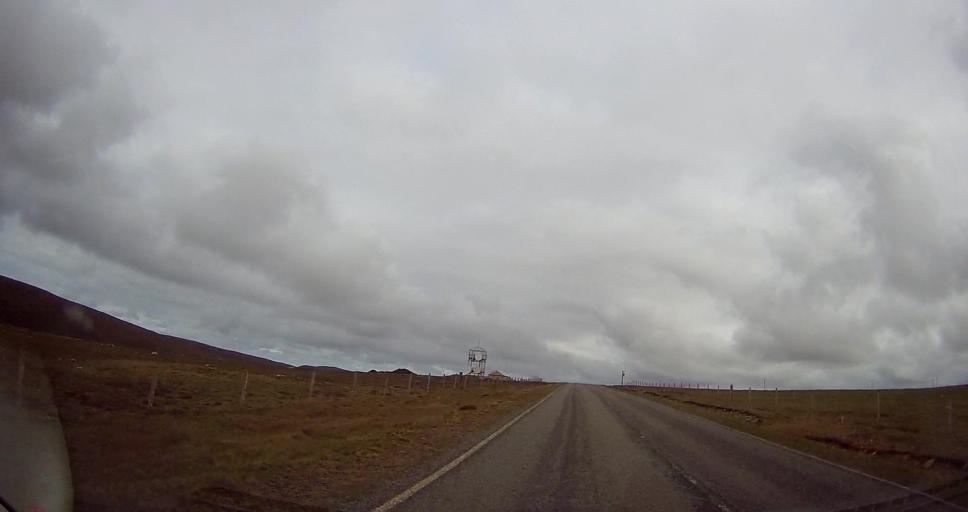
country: GB
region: Scotland
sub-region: Shetland Islands
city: Shetland
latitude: 60.7351
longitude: -0.8946
